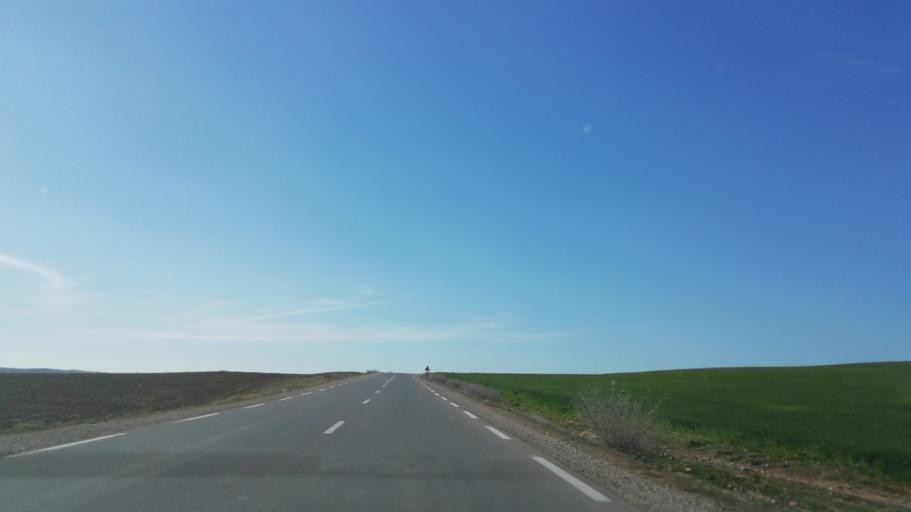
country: DZ
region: Mascara
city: Oued el Abtal
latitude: 35.4471
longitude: 0.8171
